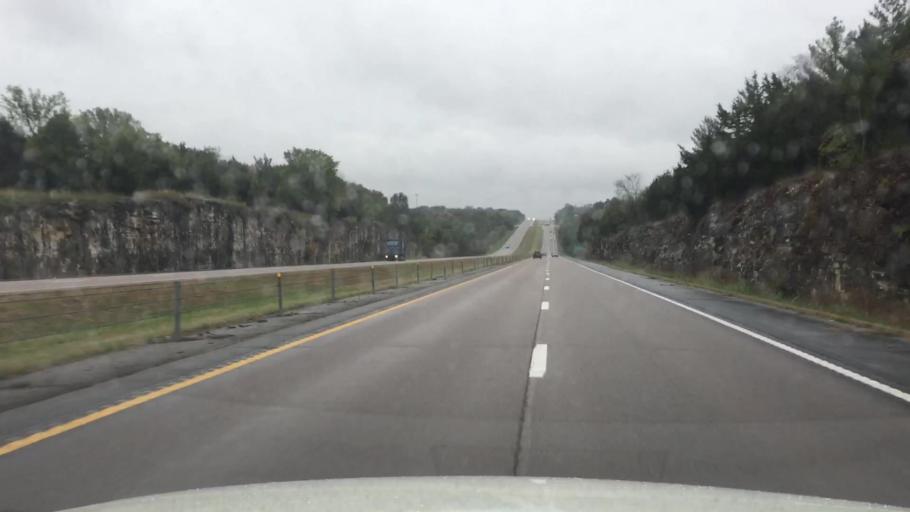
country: US
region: Missouri
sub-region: Boone County
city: Ashland
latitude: 38.7072
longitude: -92.2547
